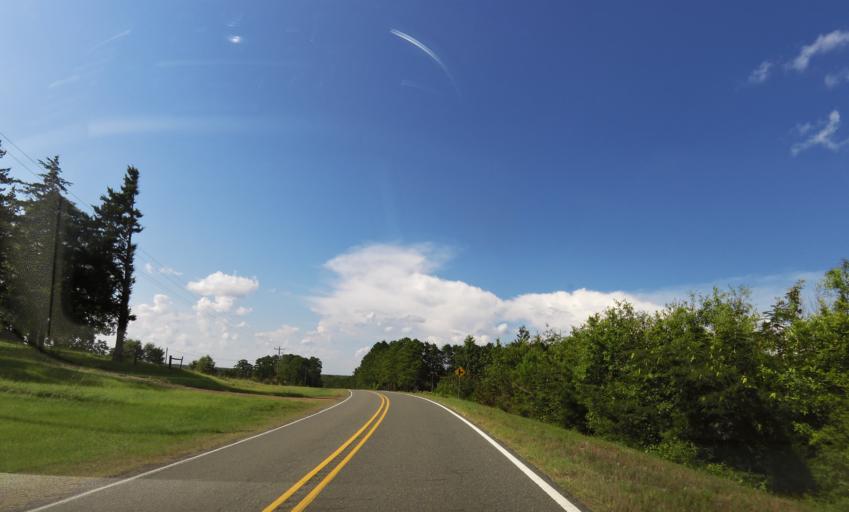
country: US
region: Louisiana
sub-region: Sabine Parish
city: Many
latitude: 31.4531
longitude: -93.5758
